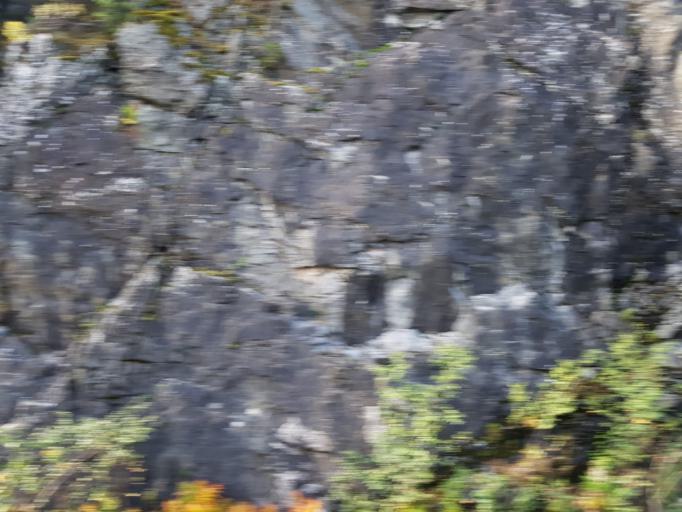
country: NO
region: Sor-Trondelag
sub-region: Trondheim
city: Trondheim
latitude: 63.4536
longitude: 10.3052
